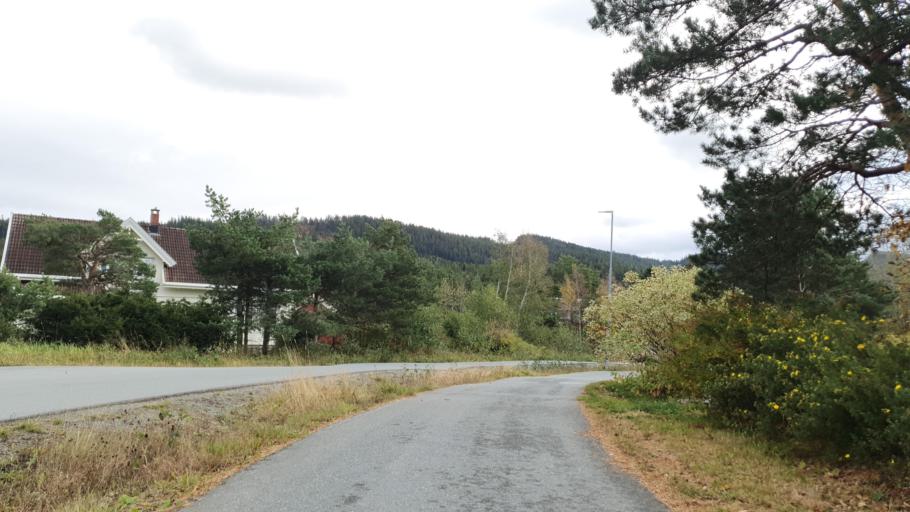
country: NO
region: Sor-Trondelag
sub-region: Klaebu
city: Klaebu
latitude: 63.3037
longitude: 10.4822
